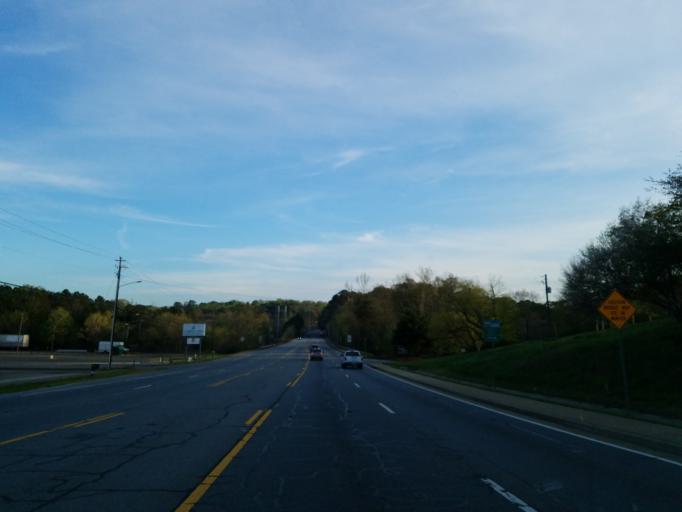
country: US
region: Georgia
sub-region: Cherokee County
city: Canton
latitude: 34.2312
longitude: -84.5001
